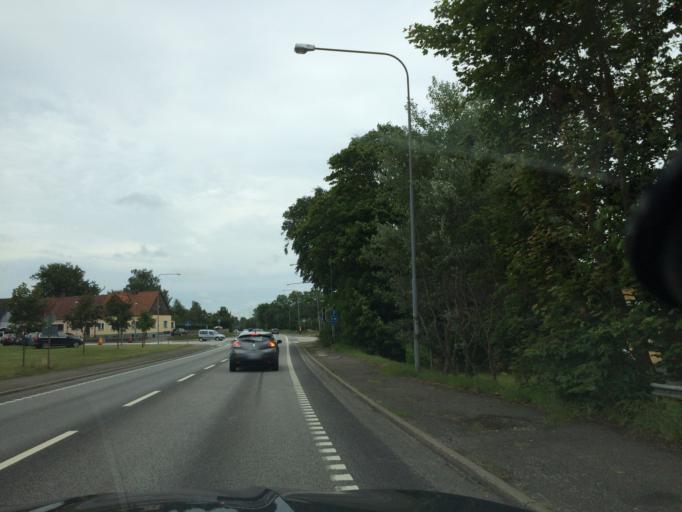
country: SE
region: Skane
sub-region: Tomelilla Kommun
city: Tomelilla
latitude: 55.5478
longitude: 13.9512
